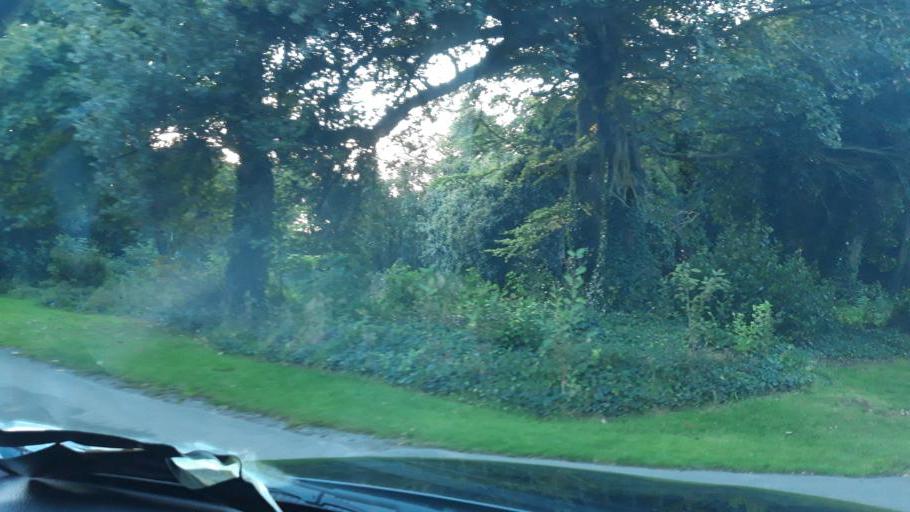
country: IE
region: Leinster
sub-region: Fingal County
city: Howth
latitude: 53.3868
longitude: -6.0793
